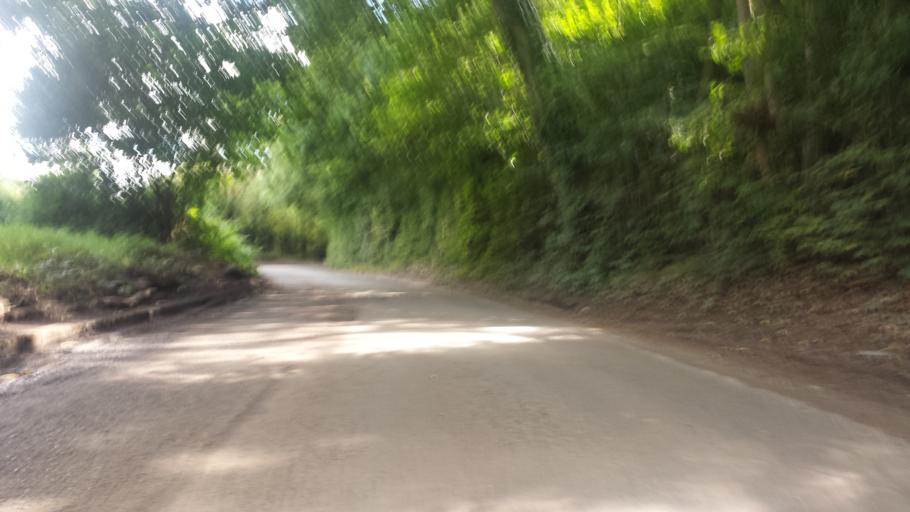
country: GB
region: England
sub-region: Kent
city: Swanley
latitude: 51.3953
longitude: 0.1428
